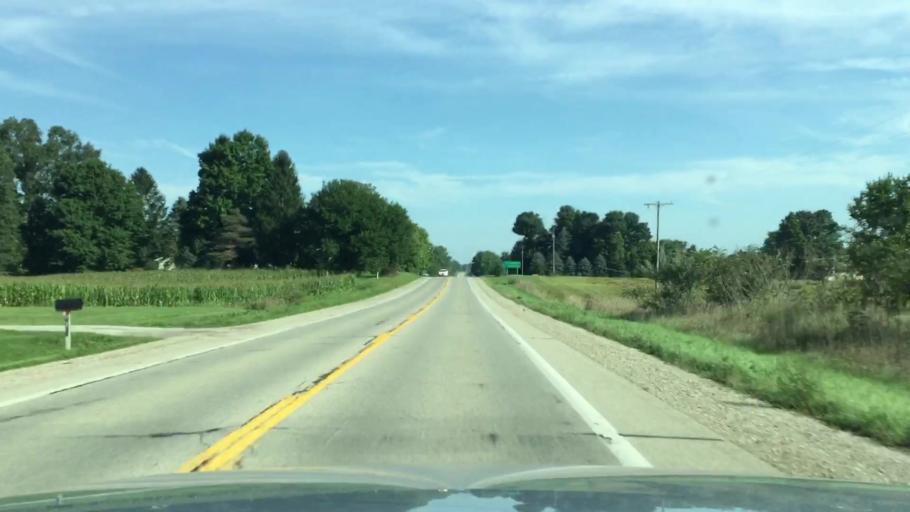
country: US
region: Michigan
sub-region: Lenawee County
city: Hudson
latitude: 41.9392
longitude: -84.3671
